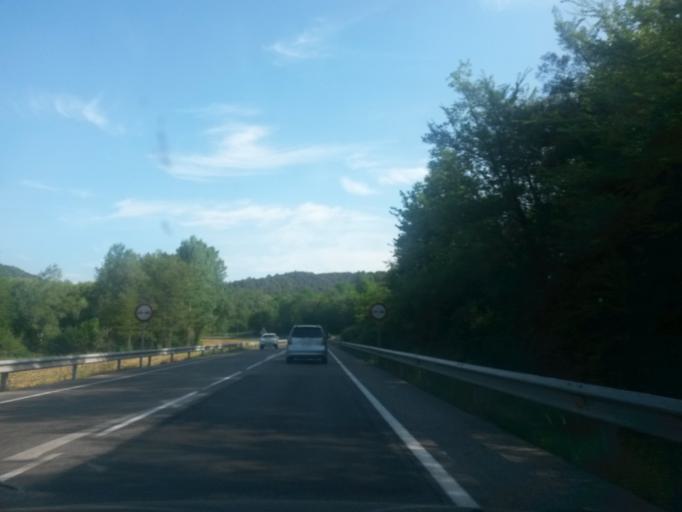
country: ES
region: Catalonia
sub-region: Provincia de Girona
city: Sant Feliu de Pallerols
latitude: 42.1005
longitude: 2.4956
